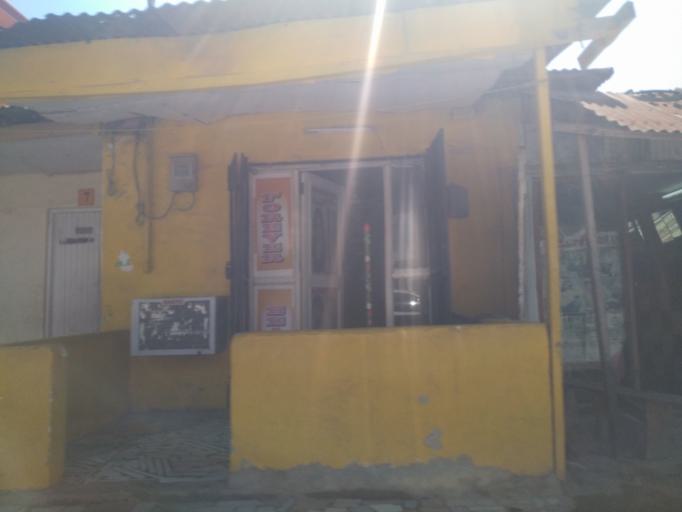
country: TZ
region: Dar es Salaam
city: Magomeni
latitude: -6.7905
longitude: 39.2650
